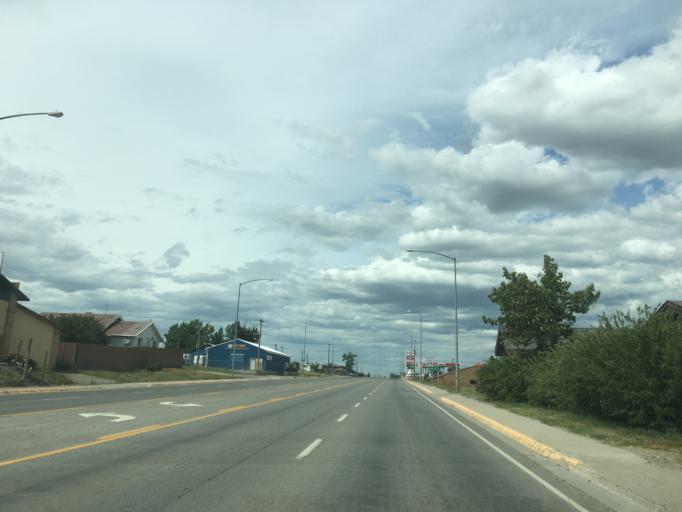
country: US
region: Montana
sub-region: Glacier County
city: Browning
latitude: 48.5515
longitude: -113.0098
